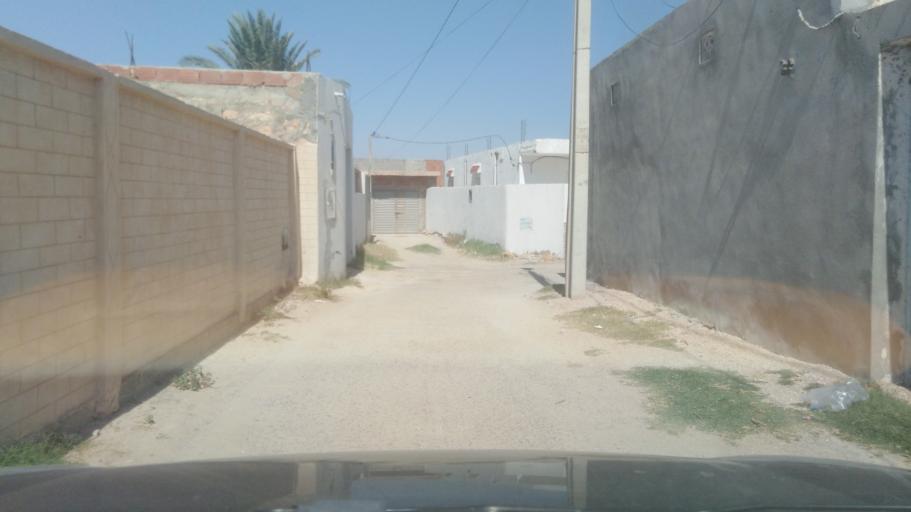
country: TN
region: Qabis
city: Gabes
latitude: 33.9589
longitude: 10.0163
